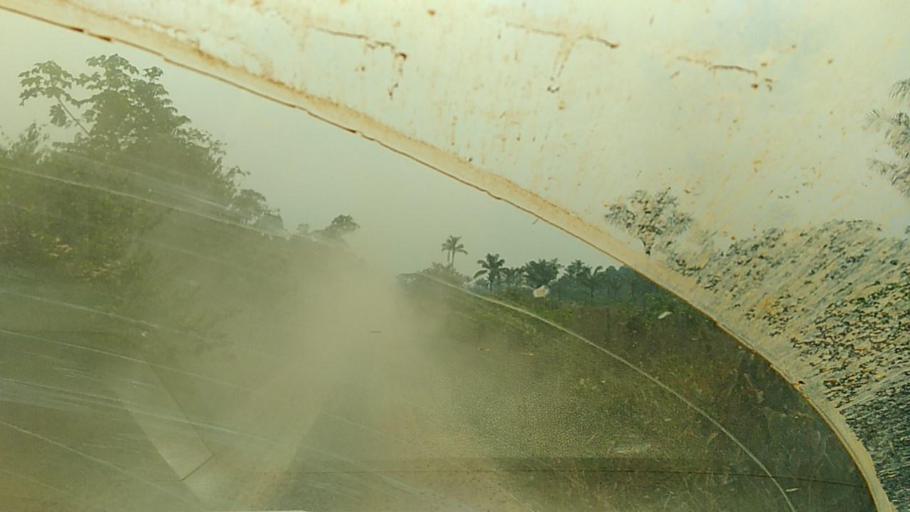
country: BR
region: Rondonia
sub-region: Porto Velho
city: Porto Velho
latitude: -8.7737
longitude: -63.1811
